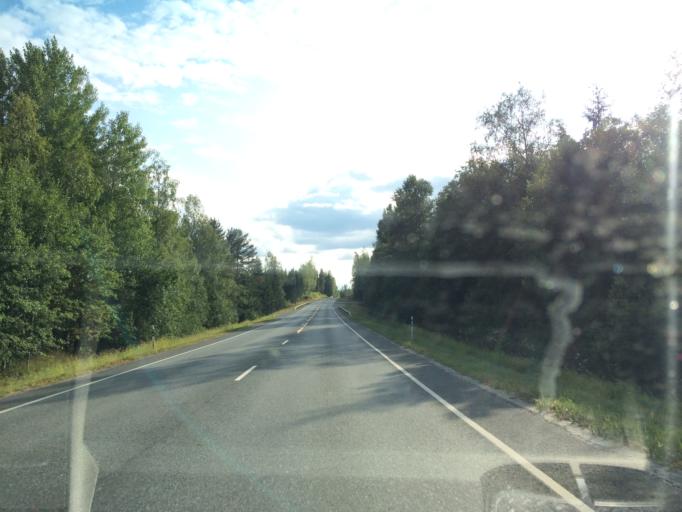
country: FI
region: Haeme
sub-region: Haemeenlinna
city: Haemeenlinna
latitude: 60.9428
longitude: 24.3888
